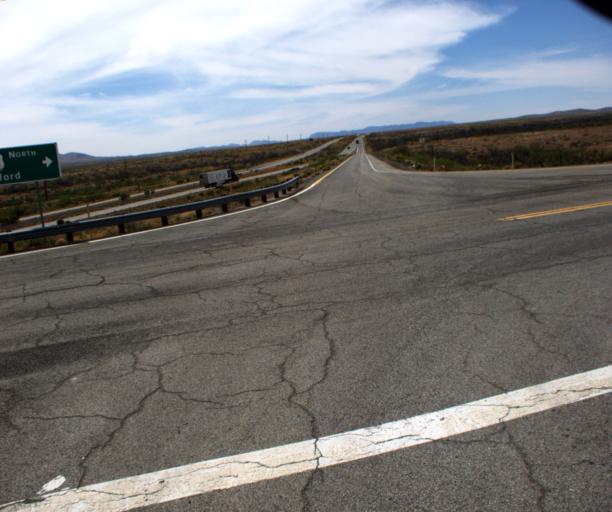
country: US
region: Arizona
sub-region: Cochise County
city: Willcox
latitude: 32.3632
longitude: -109.6212
